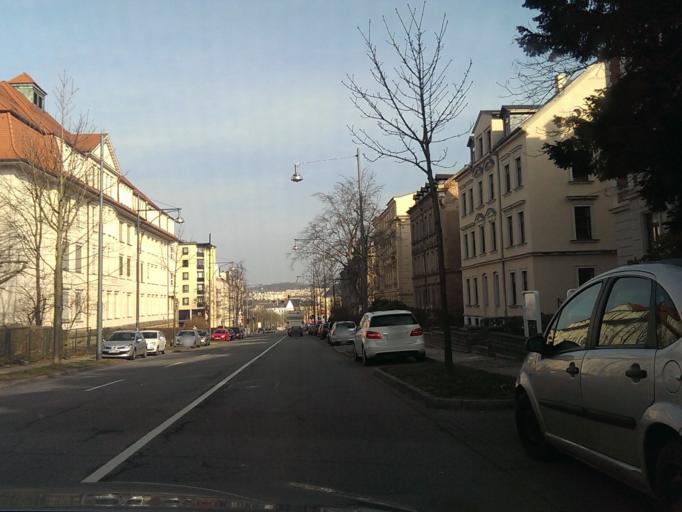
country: DE
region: Saxony
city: Chemnitz
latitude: 50.8348
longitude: 12.9074
